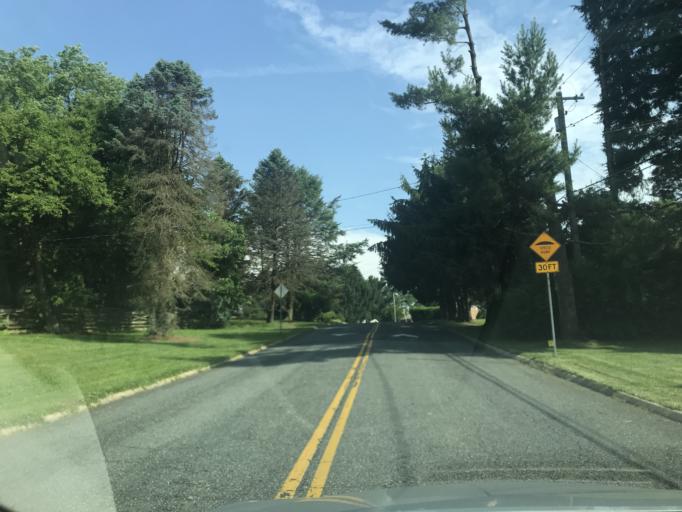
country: US
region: Maryland
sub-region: Harford County
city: Bel Air North
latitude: 39.5574
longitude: -76.3936
